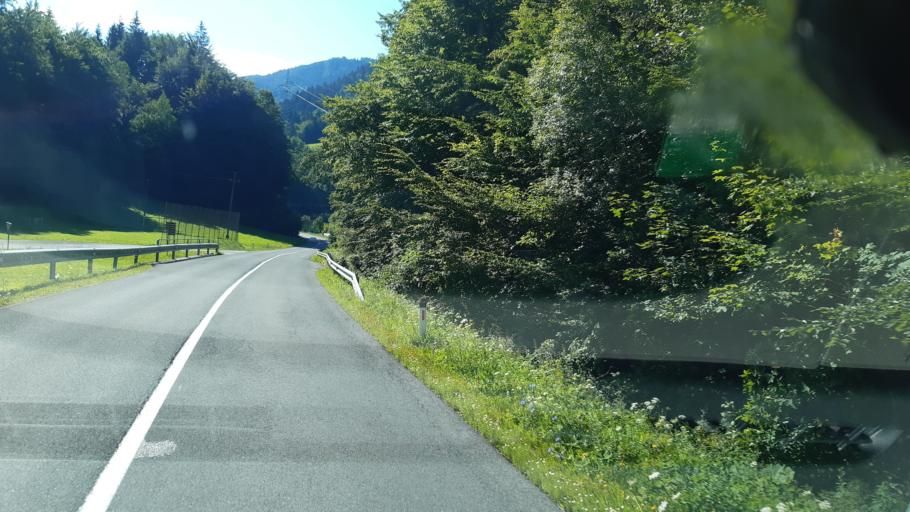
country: SI
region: Gornji Grad
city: Gornji Grad
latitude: 46.2159
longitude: 14.8449
